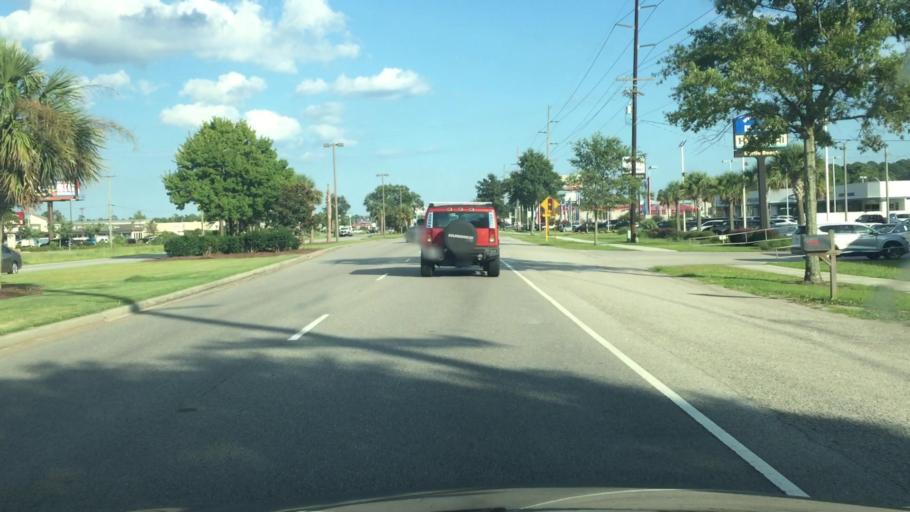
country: US
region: South Carolina
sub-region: Horry County
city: Myrtle Beach
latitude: 33.7036
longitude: -78.9067
